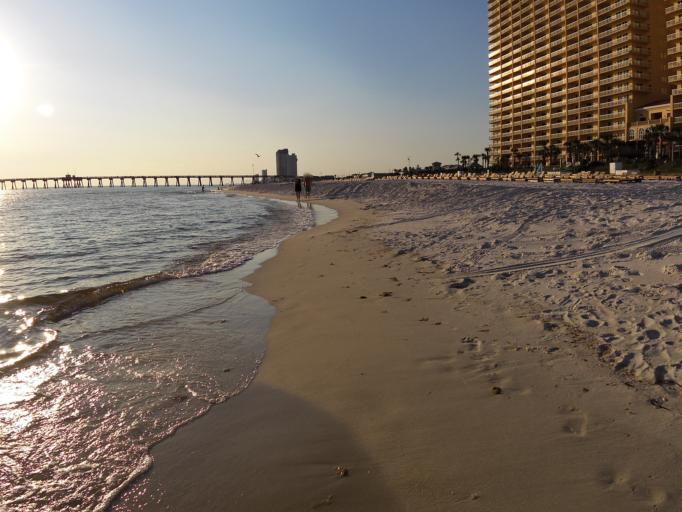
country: US
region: Florida
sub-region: Bay County
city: Laguna Beach
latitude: 30.2129
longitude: -85.8739
